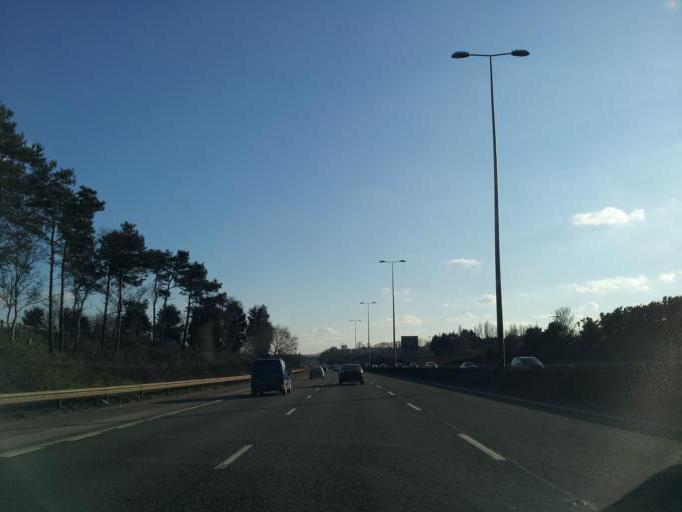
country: GB
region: England
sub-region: Devon
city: Topsham
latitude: 50.7067
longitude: -3.4673
